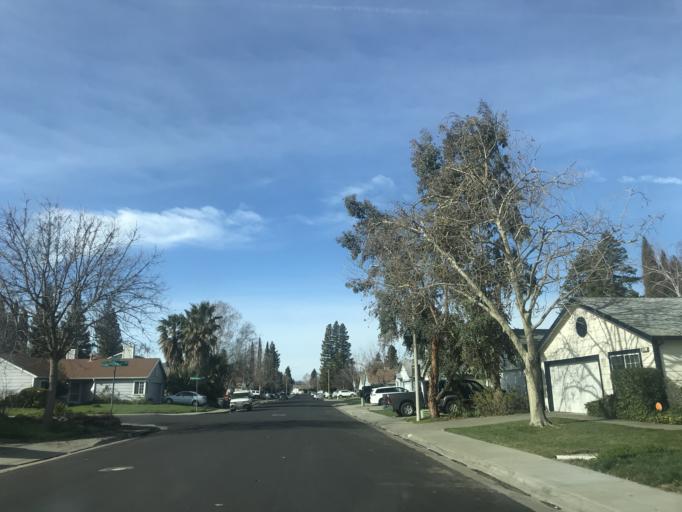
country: US
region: California
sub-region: Yolo County
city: Woodland
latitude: 38.6602
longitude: -121.7543
